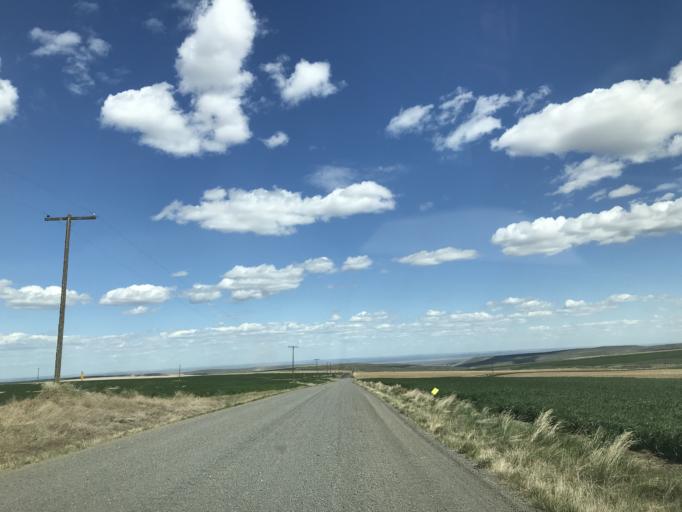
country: US
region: Washington
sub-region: Grant County
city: Ephrata
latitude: 47.3374
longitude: -119.7094
